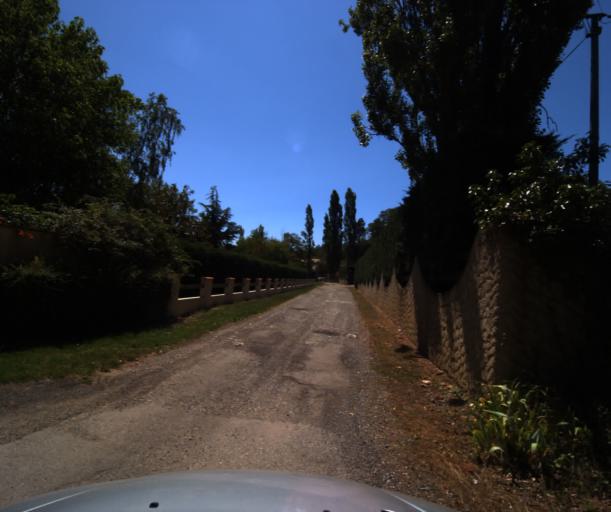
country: FR
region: Midi-Pyrenees
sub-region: Departement de la Haute-Garonne
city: Muret
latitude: 43.4533
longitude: 1.3440
